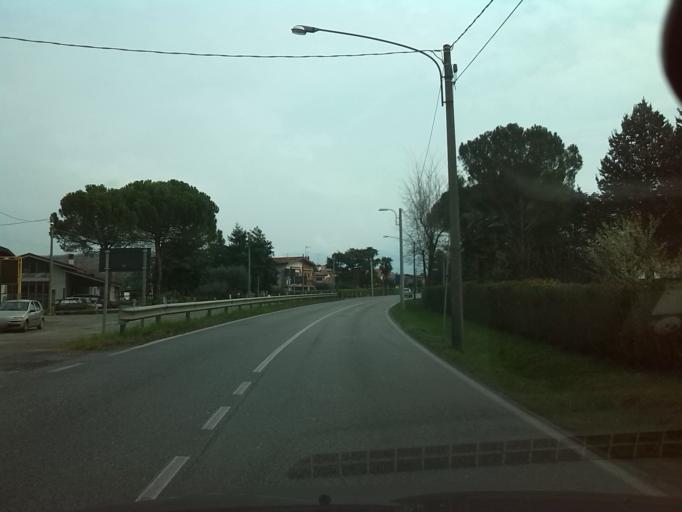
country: IT
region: Friuli Venezia Giulia
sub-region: Provincia di Gorizia
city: Mossa
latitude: 45.9362
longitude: 13.5589
